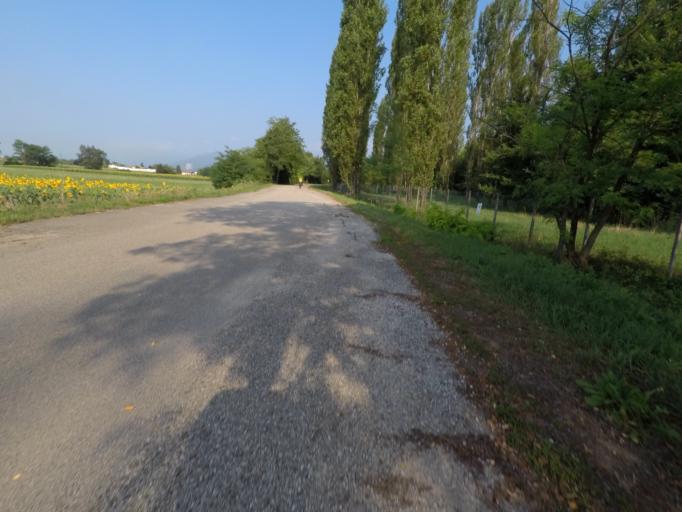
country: IT
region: Friuli Venezia Giulia
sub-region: Provincia di Pordenone
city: Travesio
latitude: 46.2013
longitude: 12.8431
